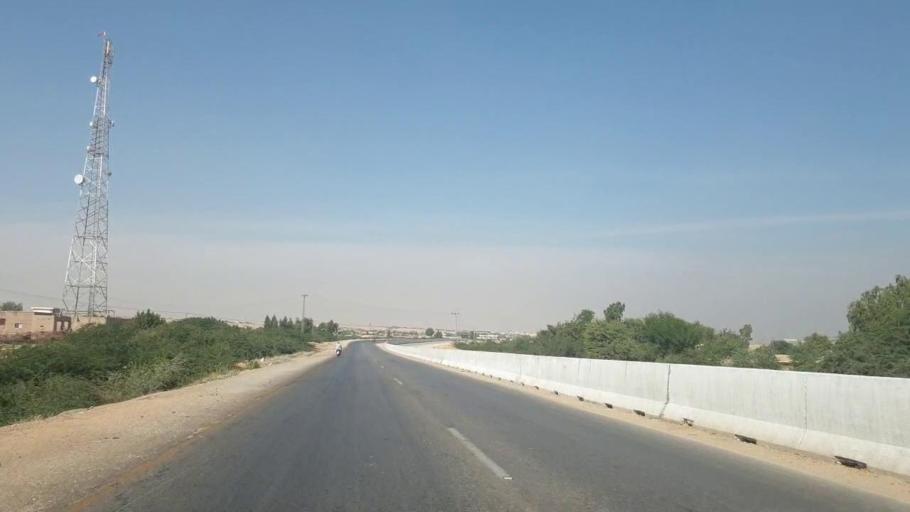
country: PK
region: Sindh
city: Hala
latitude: 25.7177
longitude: 68.2941
